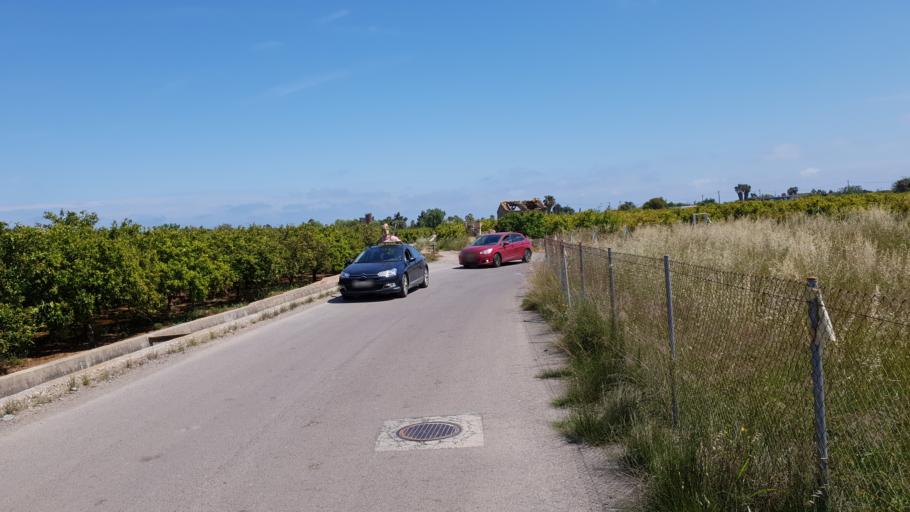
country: ES
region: Valencia
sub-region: Provincia de Castello
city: Burriana
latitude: 39.8620
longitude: -0.0890
